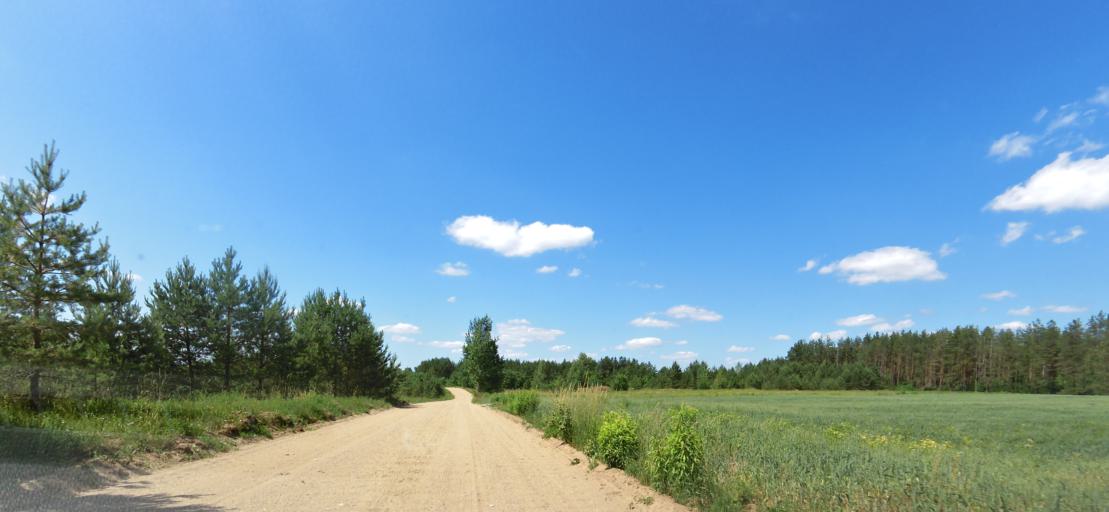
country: LT
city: Nemencine
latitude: 54.8724
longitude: 25.5541
